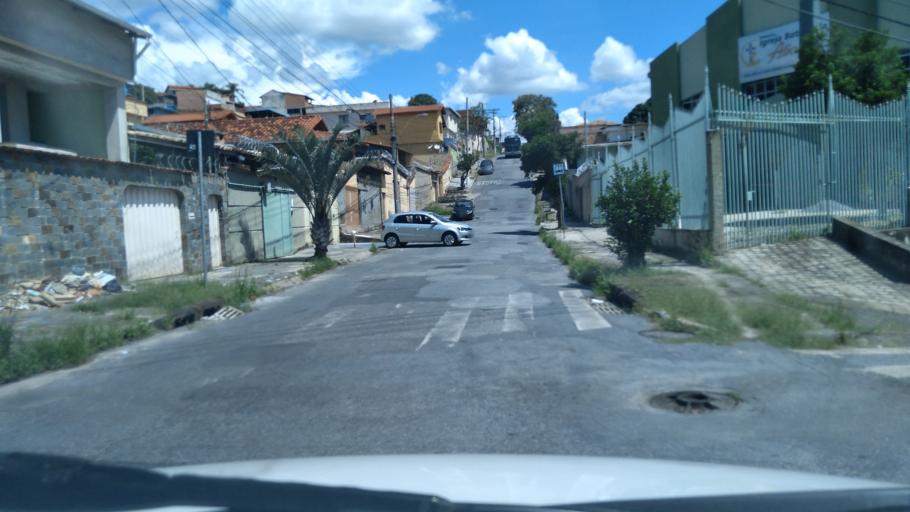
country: BR
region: Minas Gerais
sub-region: Belo Horizonte
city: Belo Horizonte
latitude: -19.8623
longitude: -43.9172
